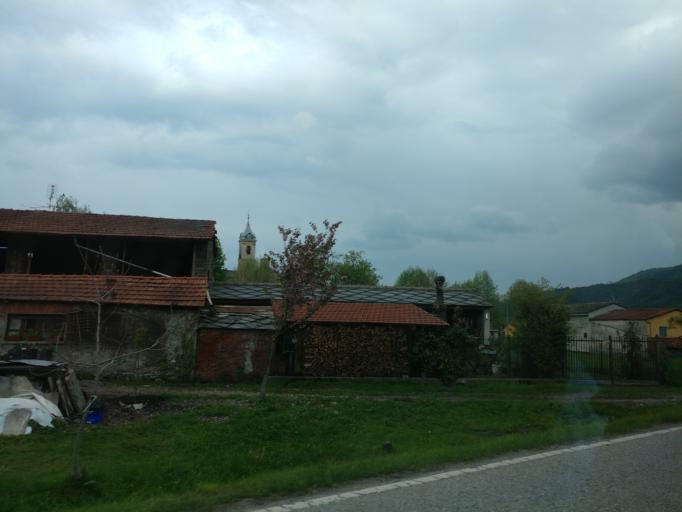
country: IT
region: Piedmont
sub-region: Provincia di Cuneo
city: Paesana
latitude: 44.6772
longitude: 7.2759
